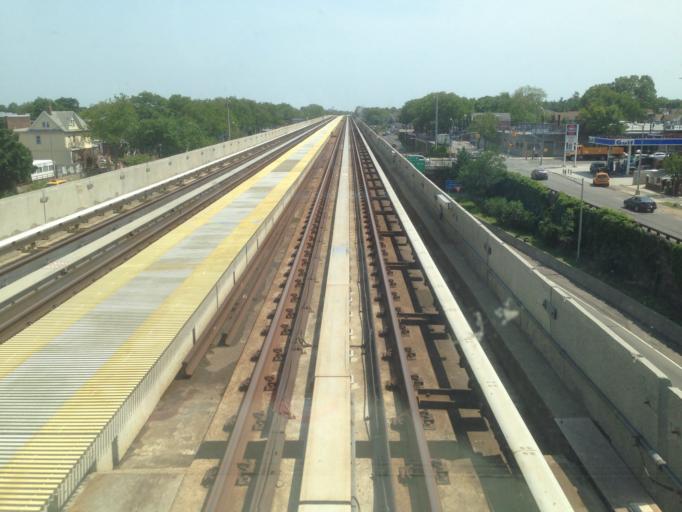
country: US
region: New York
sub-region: Queens County
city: Jamaica
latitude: 40.6951
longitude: -73.8124
